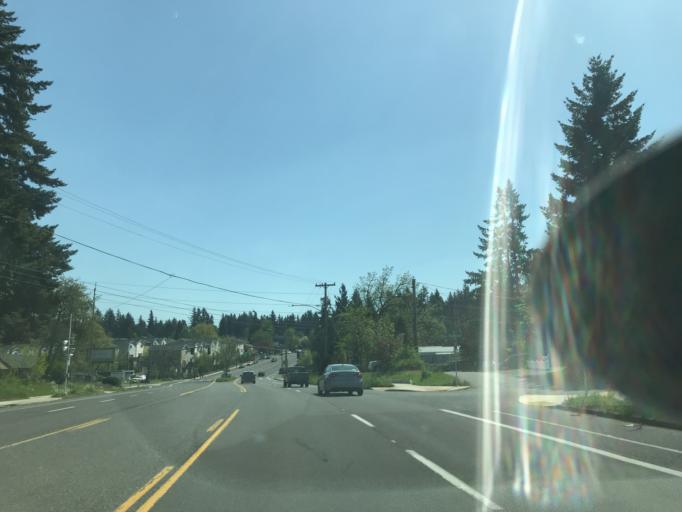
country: US
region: Oregon
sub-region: Multnomah County
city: Lents
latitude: 45.4815
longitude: -122.5379
